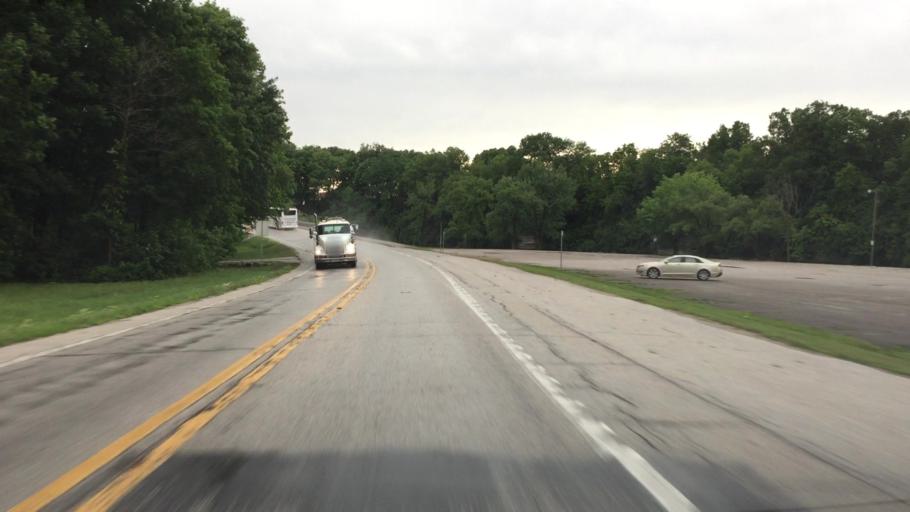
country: US
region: Illinois
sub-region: Hancock County
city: Hamilton
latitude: 40.4055
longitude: -91.3515
